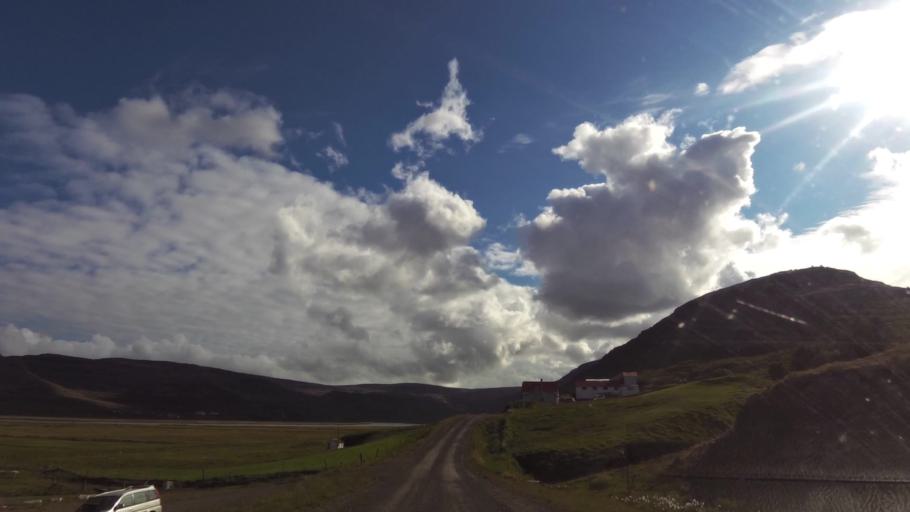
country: IS
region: West
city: Olafsvik
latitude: 65.5777
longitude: -24.1501
